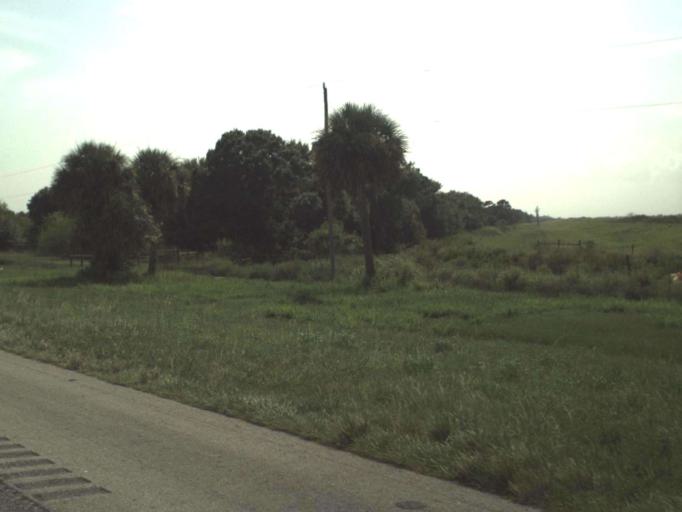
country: US
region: Florida
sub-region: Saint Lucie County
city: Fort Pierce South
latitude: 27.3890
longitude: -80.4014
